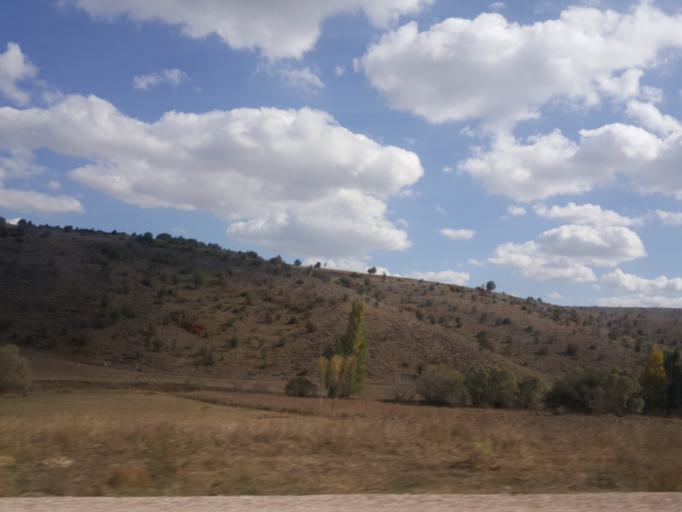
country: TR
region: Tokat
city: Camlibel
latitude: 40.1577
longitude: 36.4044
